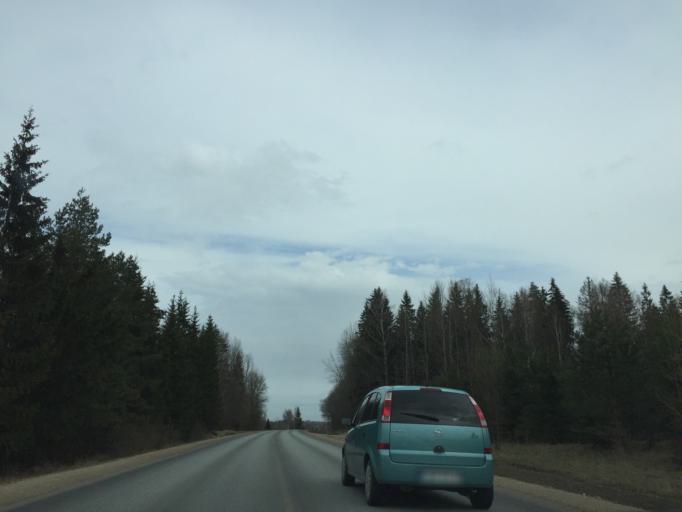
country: LV
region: Amatas Novads
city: Drabesi
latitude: 57.2393
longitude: 25.2543
